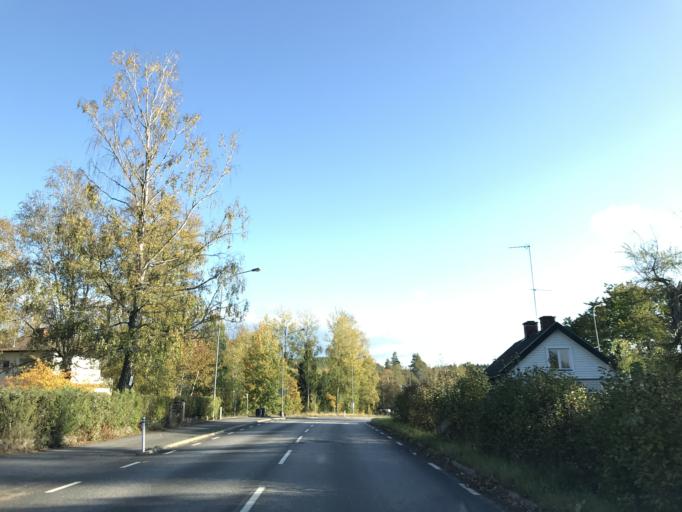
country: SE
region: Kalmar
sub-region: Hultsfreds Kommun
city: Virserum
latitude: 57.4123
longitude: 15.6179
